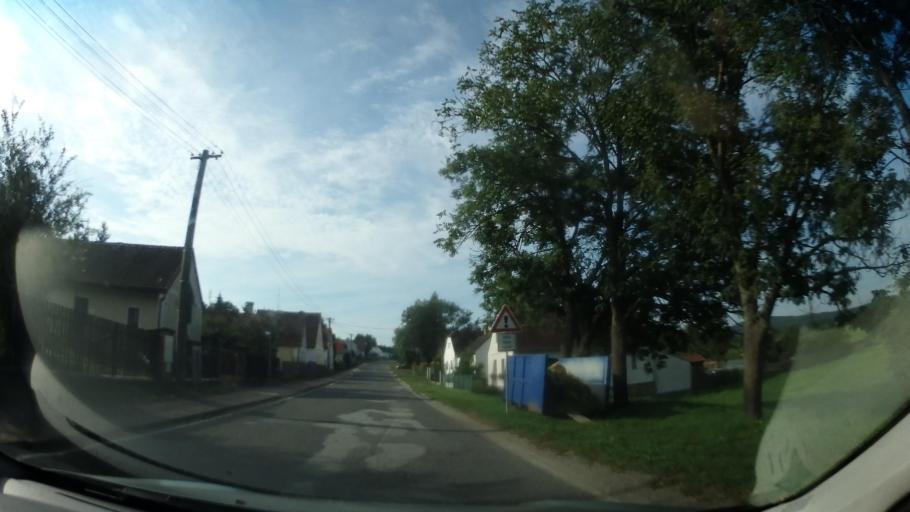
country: CZ
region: Jihocesky
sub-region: Okres Pisek
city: Pisek
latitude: 49.3902
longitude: 14.1282
